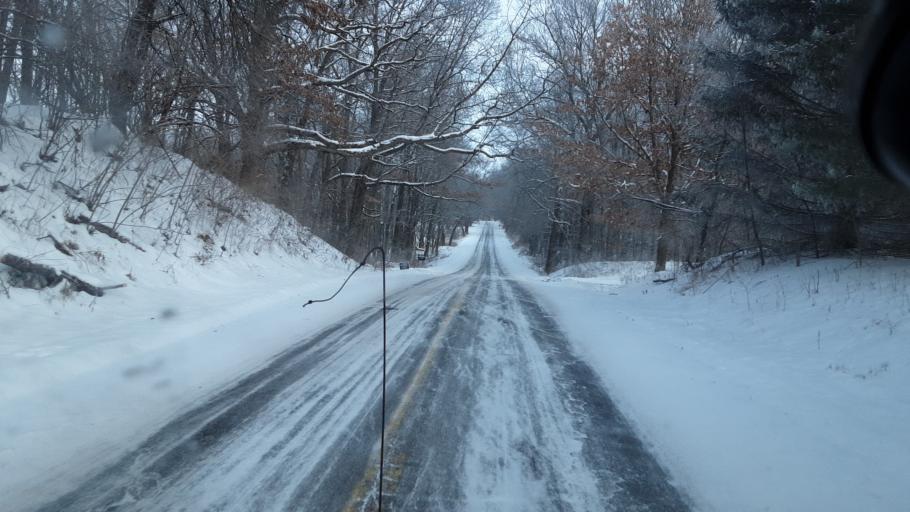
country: US
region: Michigan
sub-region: Ingham County
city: Leslie
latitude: 42.3635
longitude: -84.4826
